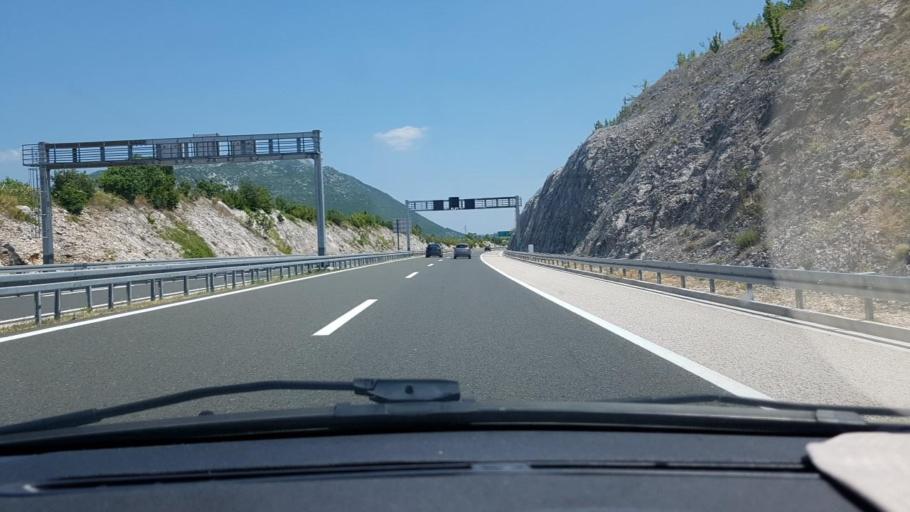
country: HR
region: Splitsko-Dalmatinska
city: Vrgorac
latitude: 43.2236
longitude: 17.2531
